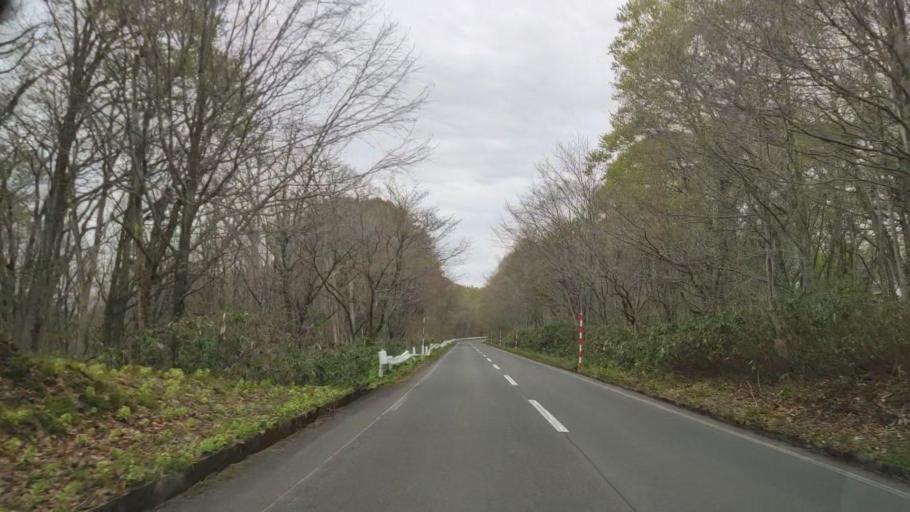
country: JP
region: Akita
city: Hanawa
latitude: 40.4037
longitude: 140.8077
